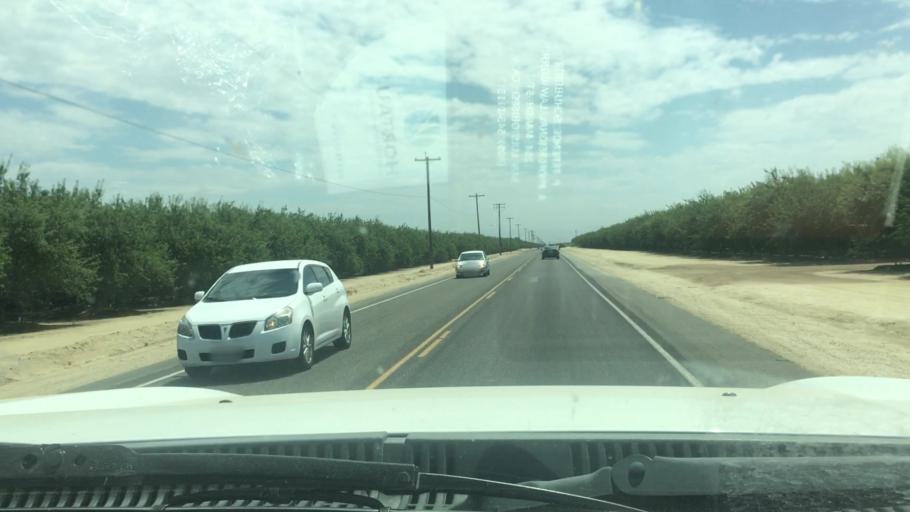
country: US
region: California
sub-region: Kern County
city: Wasco
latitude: 35.5580
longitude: -119.3195
